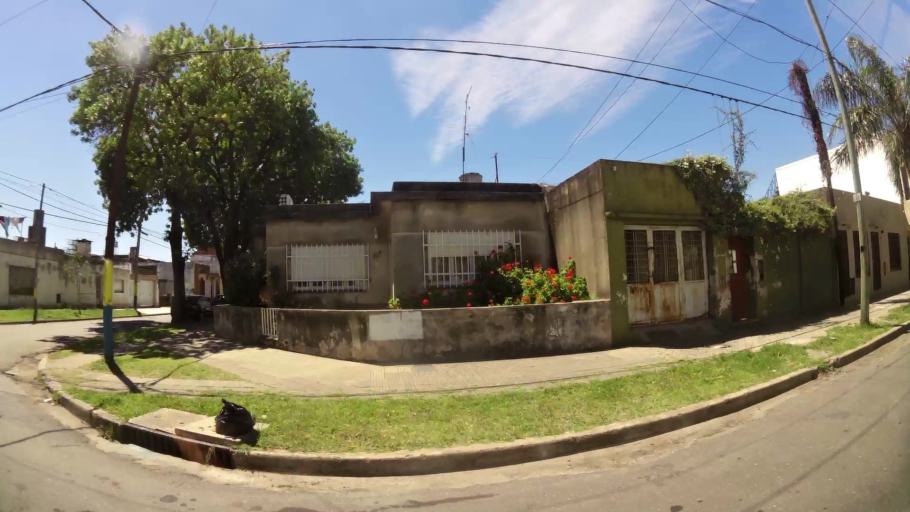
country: AR
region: Santa Fe
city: Perez
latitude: -32.9416
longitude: -60.7172
